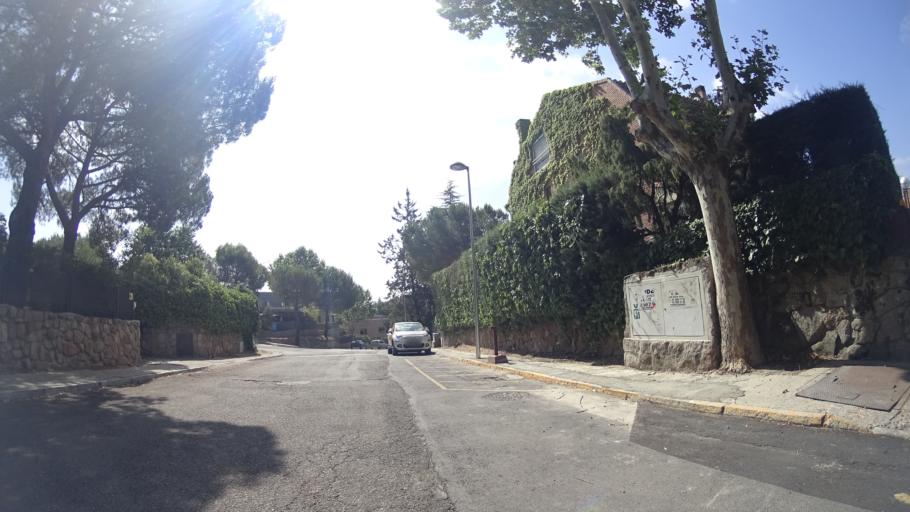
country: ES
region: Madrid
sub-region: Provincia de Madrid
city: Torrelodones
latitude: 40.5865
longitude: -3.9224
